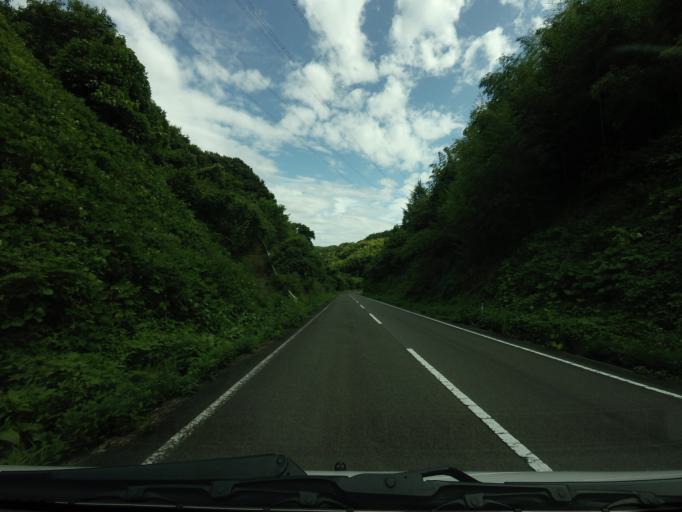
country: JP
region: Fukushima
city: Nihommatsu
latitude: 37.6381
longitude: 140.4102
